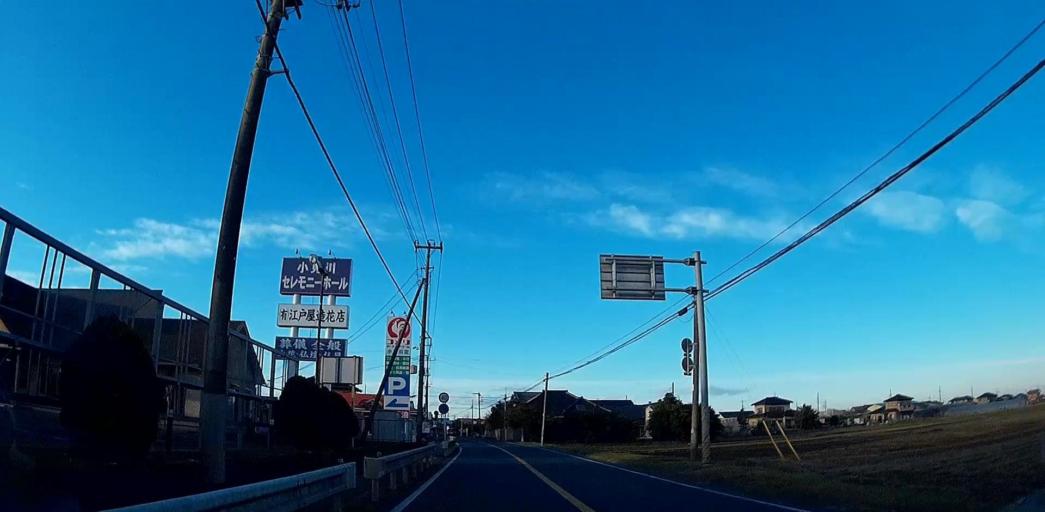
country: JP
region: Chiba
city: Omigawa
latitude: 35.8628
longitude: 140.5977
